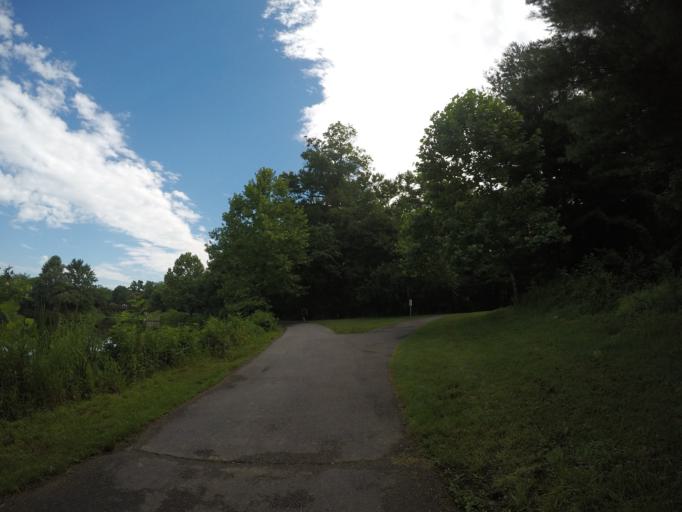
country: US
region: Maryland
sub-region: Prince George's County
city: Berwyn Heights
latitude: 38.9835
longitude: -76.9204
